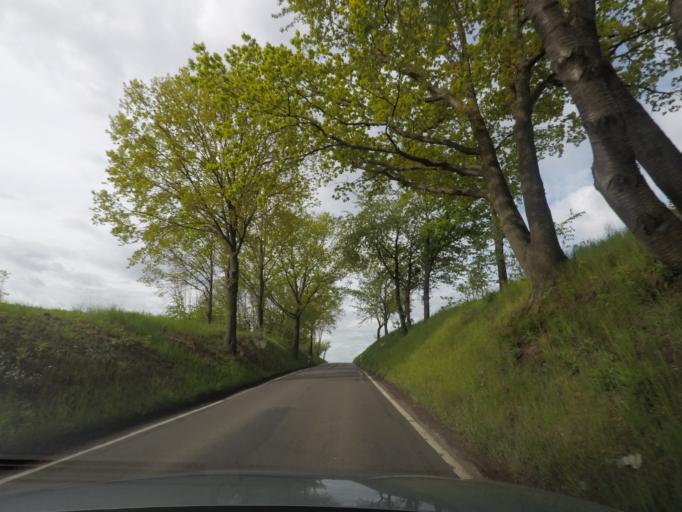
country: DE
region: Saxony
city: Ebersbach
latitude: 51.1067
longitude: 13.1107
